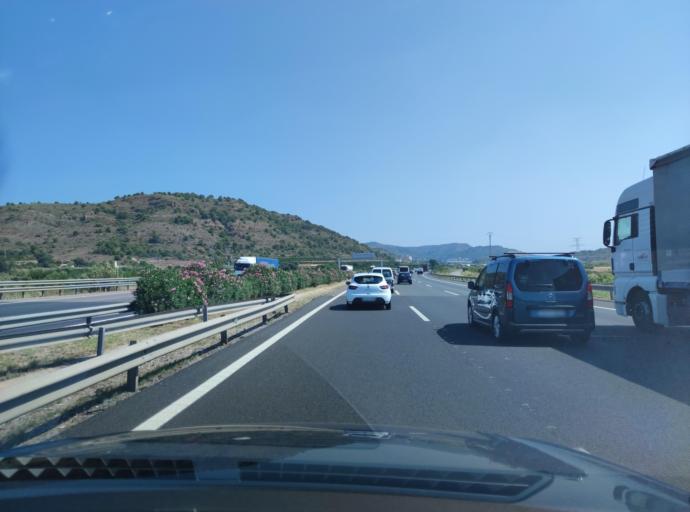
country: ES
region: Valencia
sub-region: Provincia de Valencia
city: Petres
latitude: 39.6789
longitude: -0.2997
